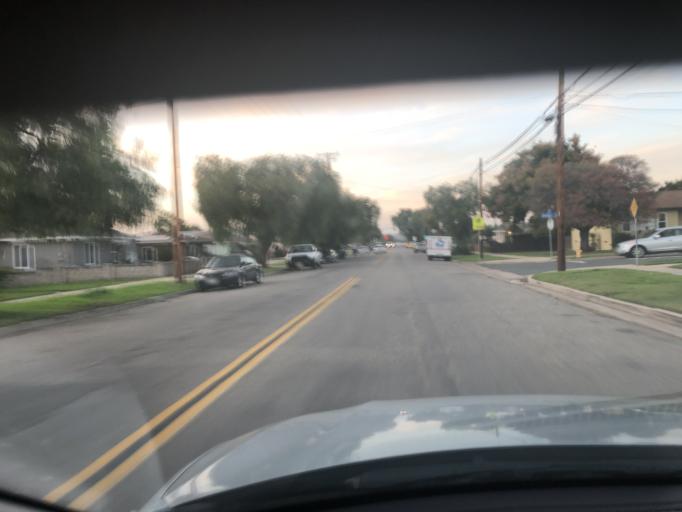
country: US
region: California
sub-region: San Diego County
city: Chula Vista
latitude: 32.6449
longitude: -117.0722
